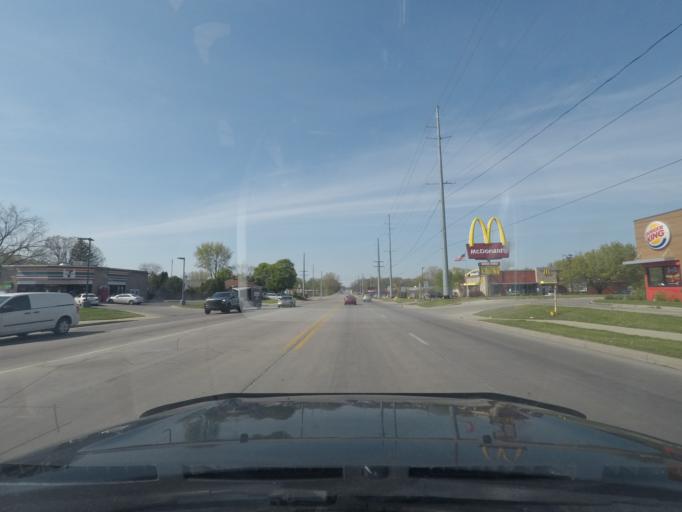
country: US
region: Indiana
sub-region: Elkhart County
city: Elkhart
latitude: 41.6745
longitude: -86.0032
